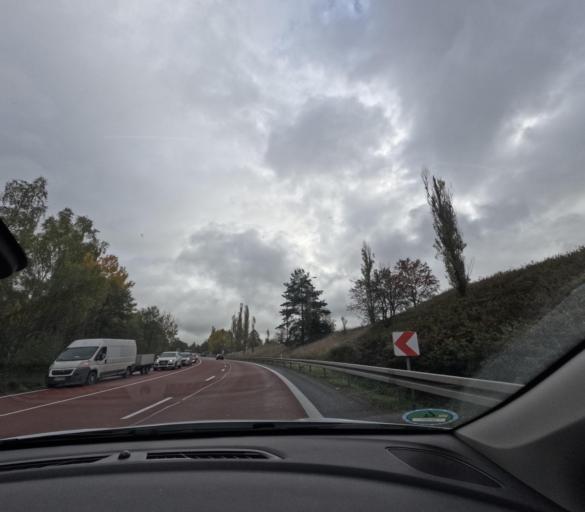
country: CZ
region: Karlovarsky
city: Dalovice
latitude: 50.2119
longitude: 12.9138
